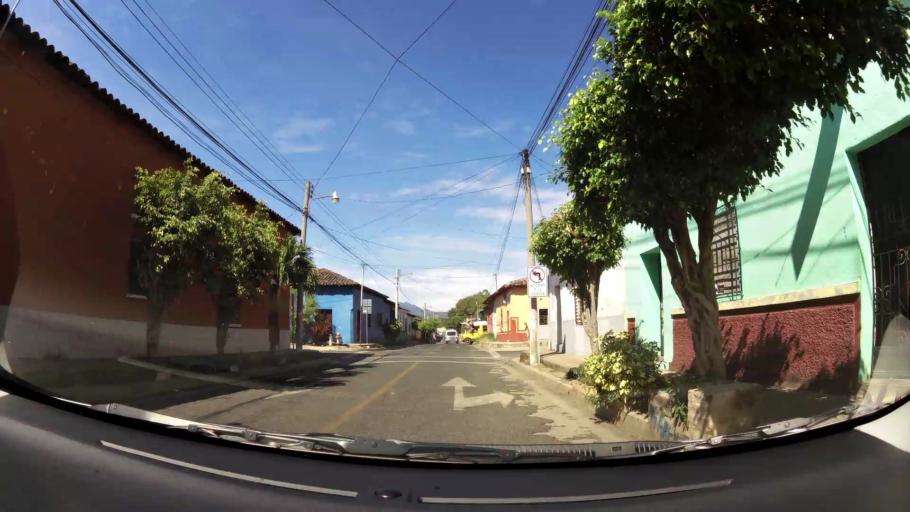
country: SV
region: Santa Ana
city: Chalchuapa
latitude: 13.9833
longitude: -89.6818
